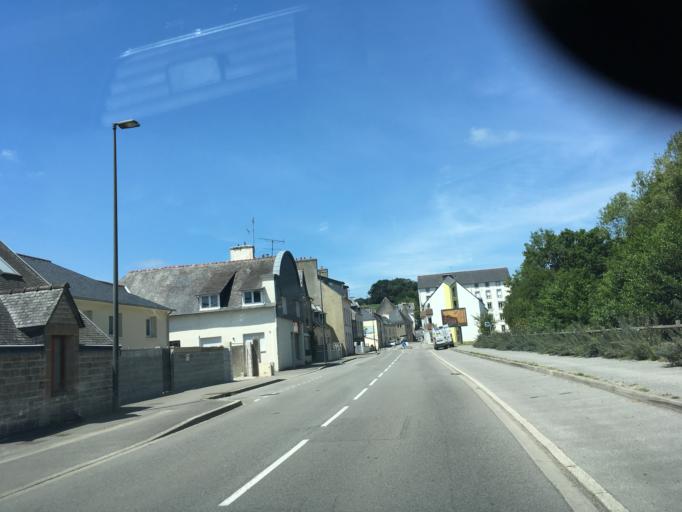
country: FR
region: Brittany
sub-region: Departement du Finistere
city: Quimper
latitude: 48.0030
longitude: -4.1147
